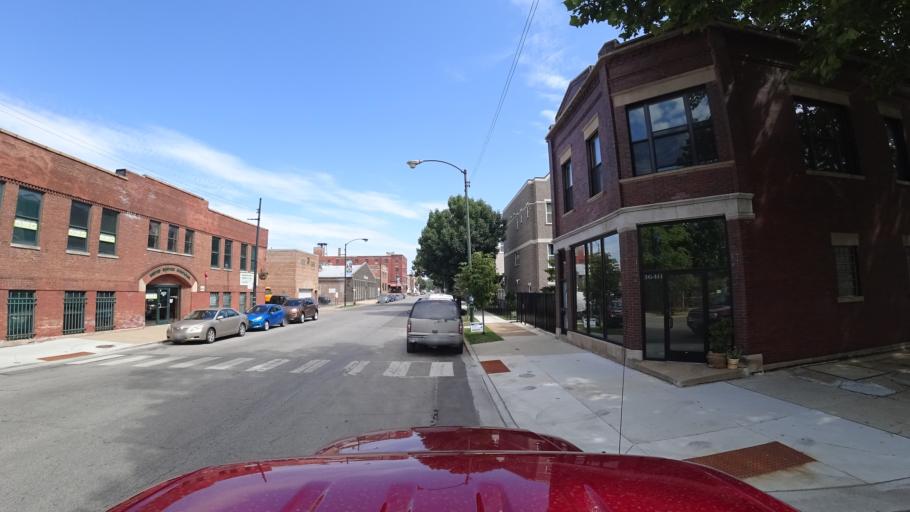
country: US
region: Illinois
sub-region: Cook County
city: Chicago
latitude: 41.8276
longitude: -87.6508
